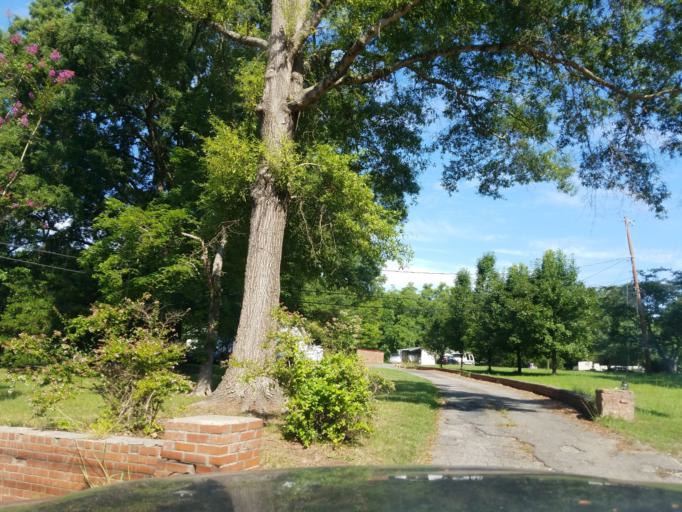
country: US
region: North Carolina
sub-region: Durham County
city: Gorman
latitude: 36.0329
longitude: -78.8276
